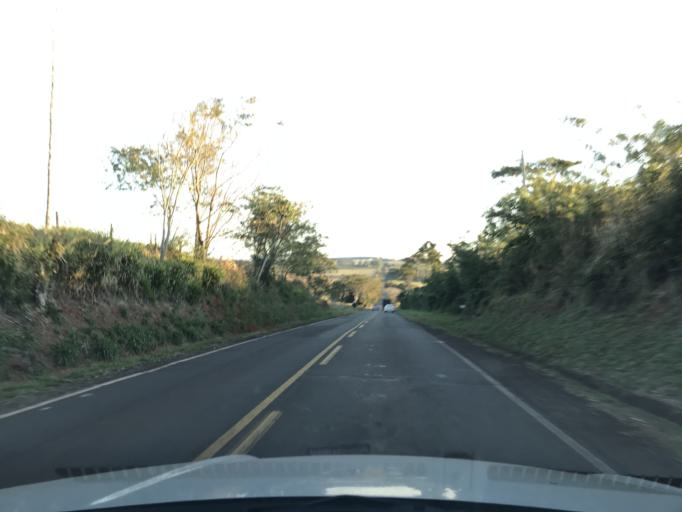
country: PY
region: Canindeyu
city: Salto del Guaira
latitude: -24.0897
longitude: -54.0932
